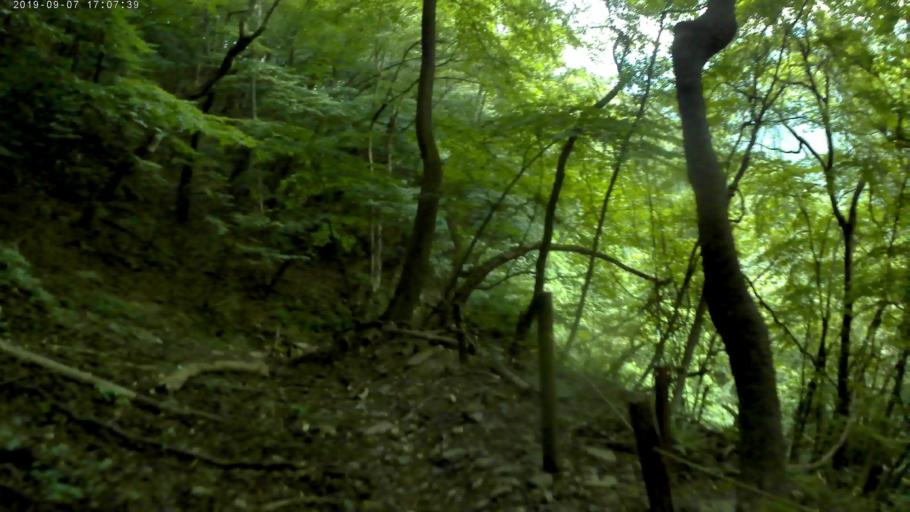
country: JP
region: Gunma
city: Annaka
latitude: 36.3591
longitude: 138.7087
